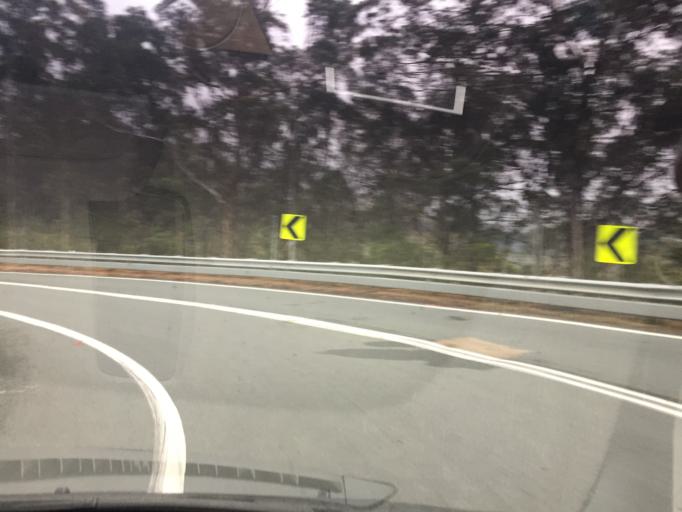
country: AU
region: New South Wales
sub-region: Bega Valley
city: Bega
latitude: -36.6127
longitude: 149.4779
